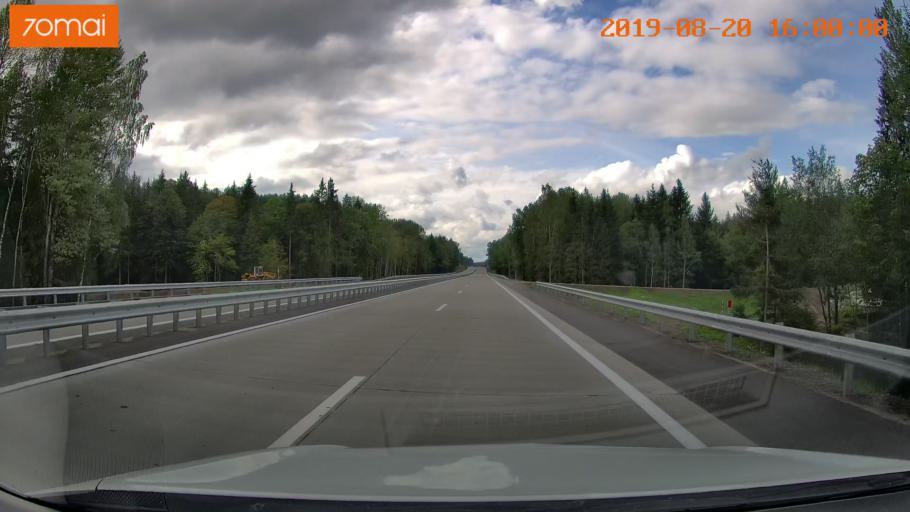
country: BY
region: Minsk
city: Korolev Stan
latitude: 54.0414
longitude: 27.8072
